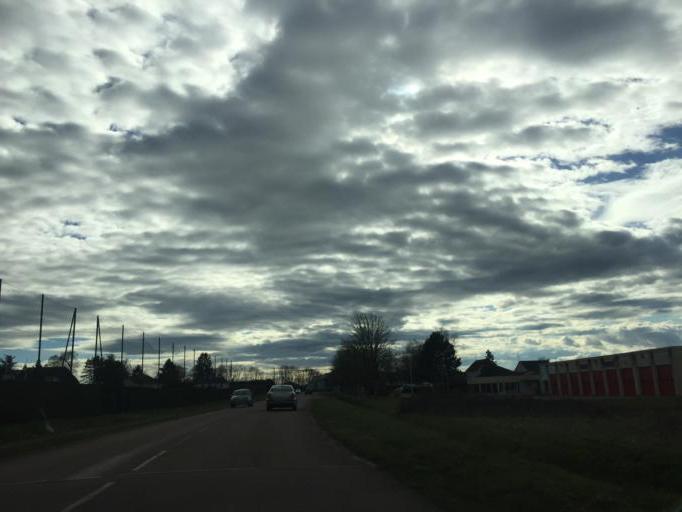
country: FR
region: Bourgogne
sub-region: Departement de l'Yonne
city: Avallon
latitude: 47.4954
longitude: 3.8975
